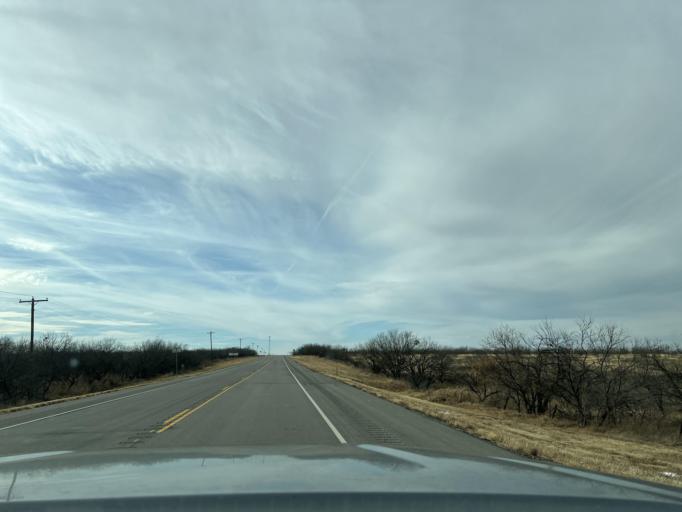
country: US
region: Texas
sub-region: Jones County
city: Anson
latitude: 32.7507
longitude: -99.7086
